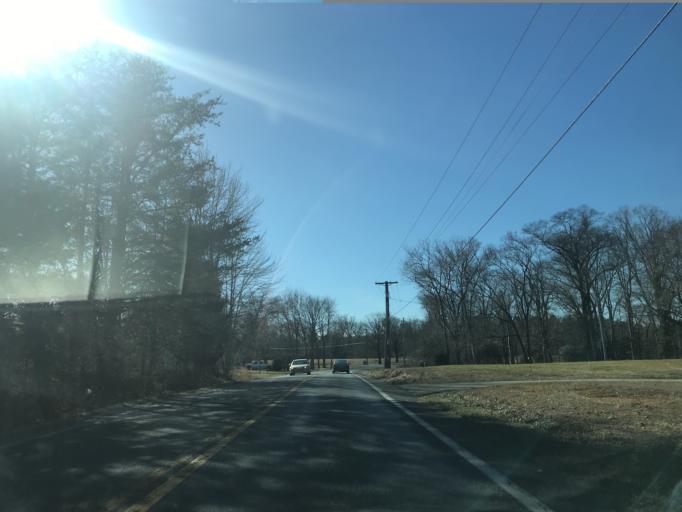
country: US
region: Maryland
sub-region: Charles County
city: Bennsville
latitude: 38.5874
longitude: -77.0110
